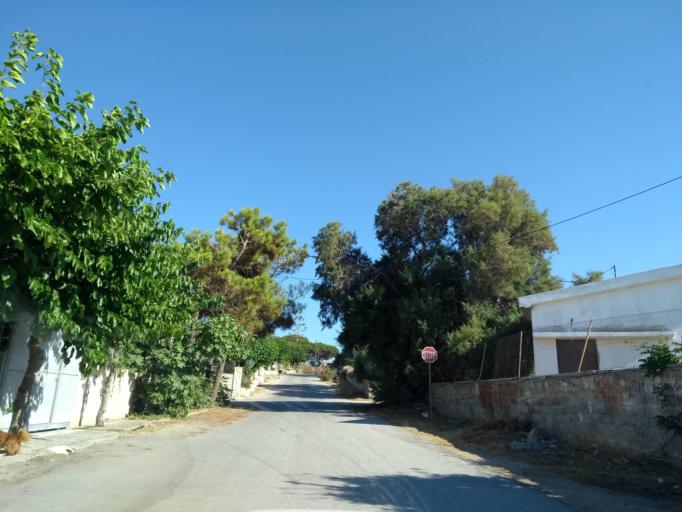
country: GR
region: Crete
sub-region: Nomos Chanias
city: Pithari
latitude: 35.5904
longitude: 24.0911
